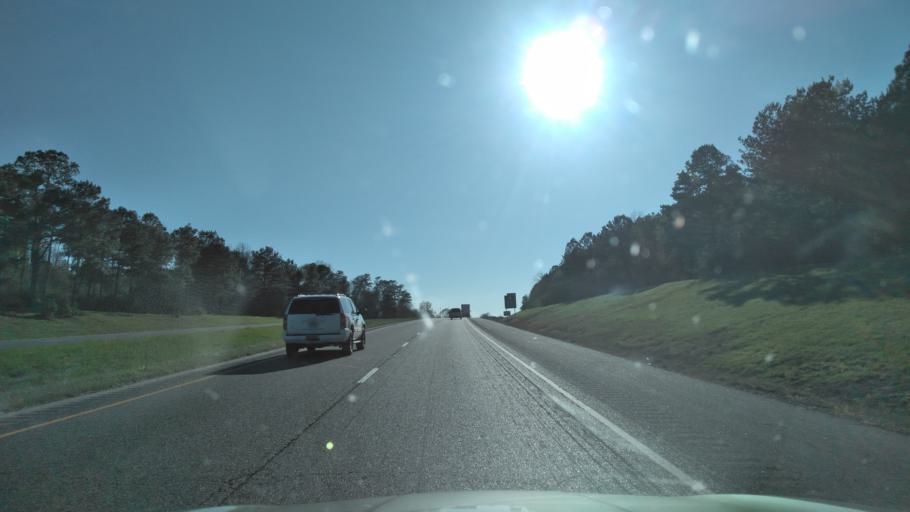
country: US
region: Alabama
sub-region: Escambia County
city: Atmore
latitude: 31.1159
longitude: -87.4596
